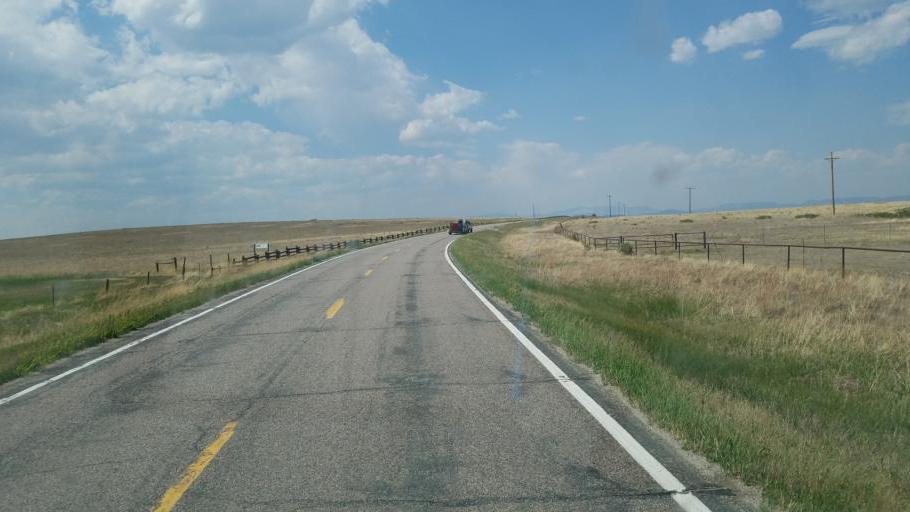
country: US
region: Colorado
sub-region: Custer County
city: Westcliffe
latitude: 38.2757
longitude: -105.6160
